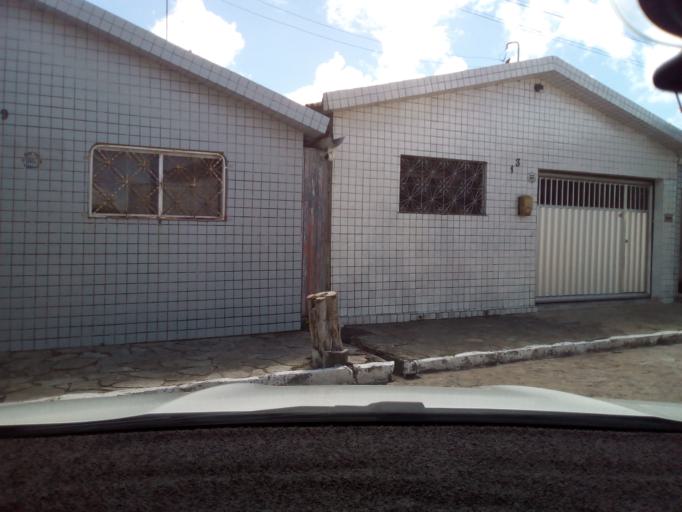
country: BR
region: Paraiba
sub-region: Cabedelo
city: Cabedelo
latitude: -6.9741
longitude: -34.8355
